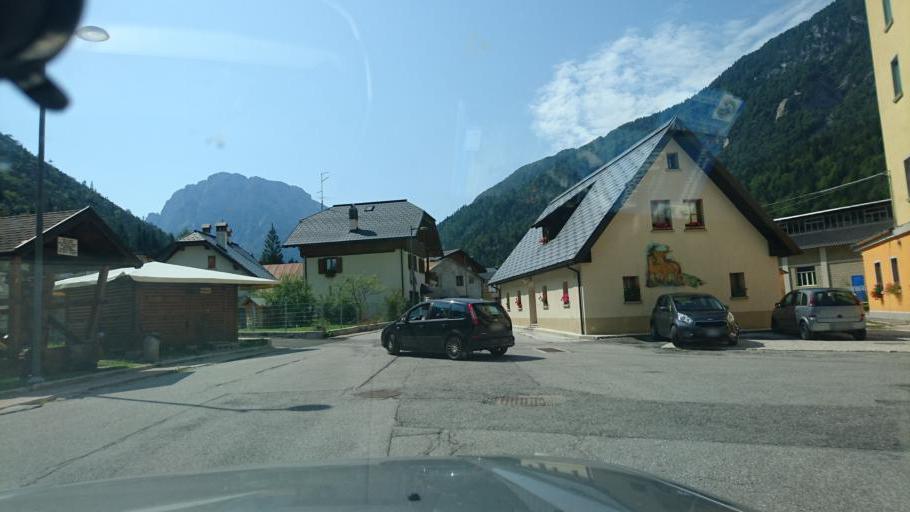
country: IT
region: Friuli Venezia Giulia
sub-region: Provincia di Udine
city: Tarvisio
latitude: 46.4405
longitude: 13.5713
